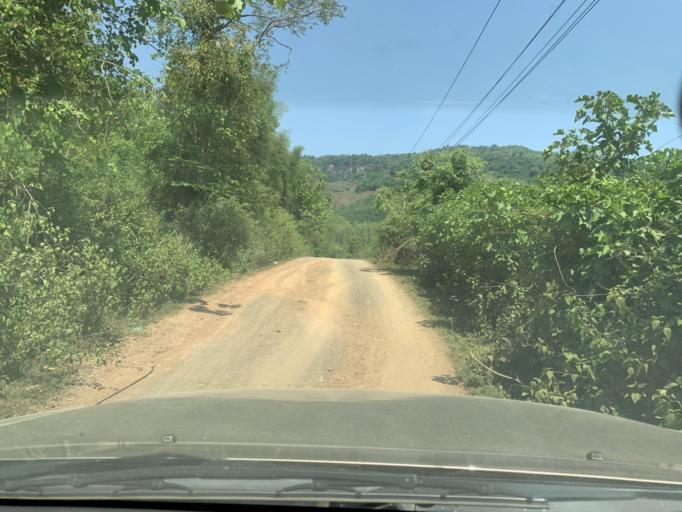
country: LA
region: Louangphabang
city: Louangphabang
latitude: 19.9139
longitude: 102.2632
